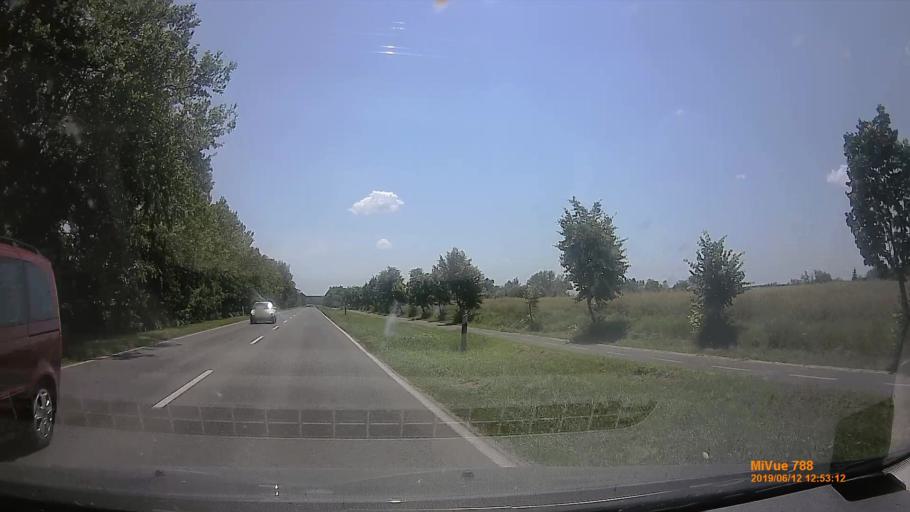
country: HU
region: Bacs-Kiskun
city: Kiskunfelegyhaza
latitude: 46.6850
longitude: 19.8516
